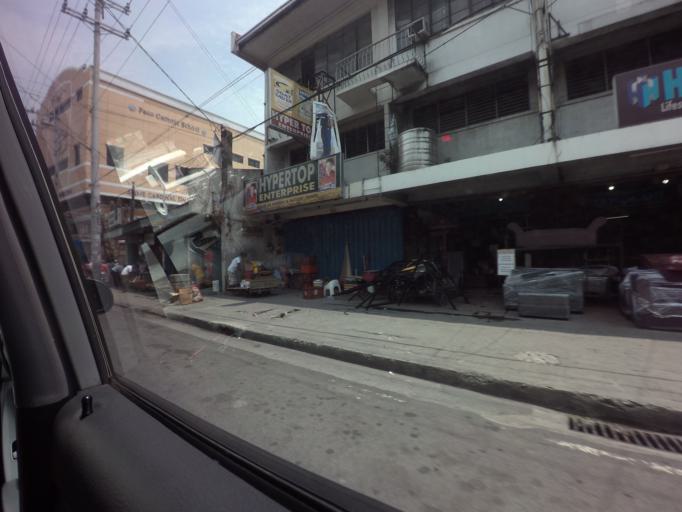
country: PH
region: Metro Manila
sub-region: City of Manila
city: Quiapo
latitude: 14.5789
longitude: 120.9955
